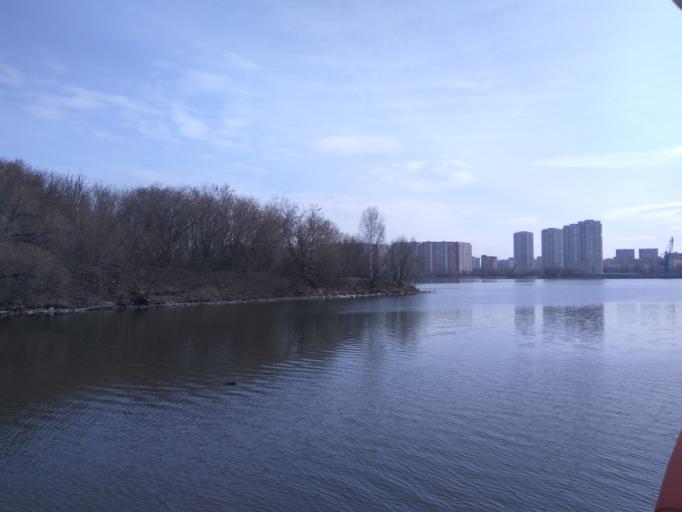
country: RU
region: Moscow
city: Kolomenskoye
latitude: 55.6899
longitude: 37.7044
